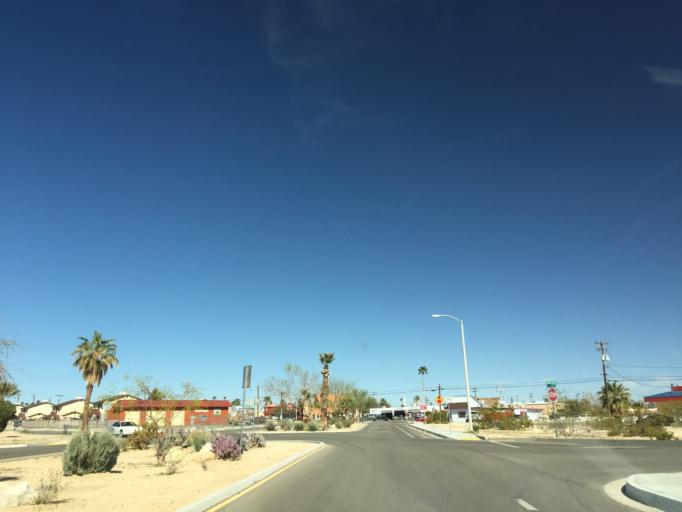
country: US
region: California
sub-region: San Bernardino County
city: Twentynine Palms
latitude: 34.1343
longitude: -116.0504
